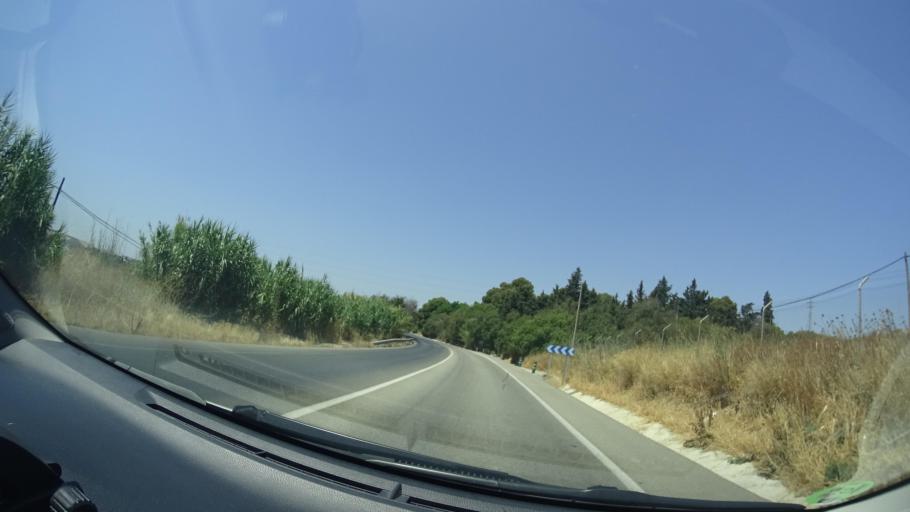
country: ES
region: Andalusia
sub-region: Provincia de Cadiz
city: Jerez de la Frontera
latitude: 36.6558
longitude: -6.0941
